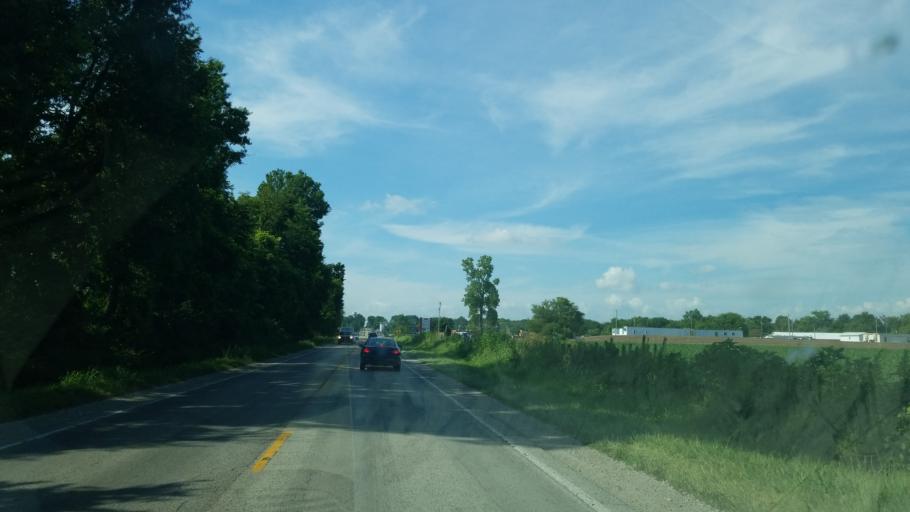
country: US
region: Illinois
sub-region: Saint Clair County
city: Lebanon
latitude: 38.5913
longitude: -89.8077
